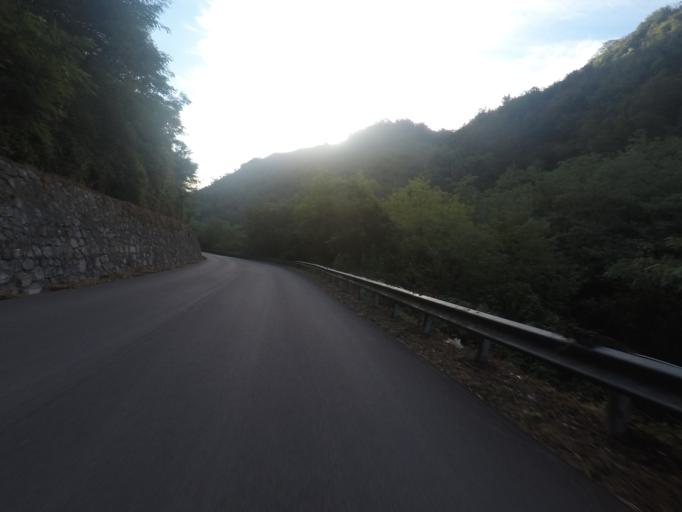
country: IT
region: Tuscany
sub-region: Provincia di Lucca
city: Valdottavo
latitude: 43.9628
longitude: 10.4652
